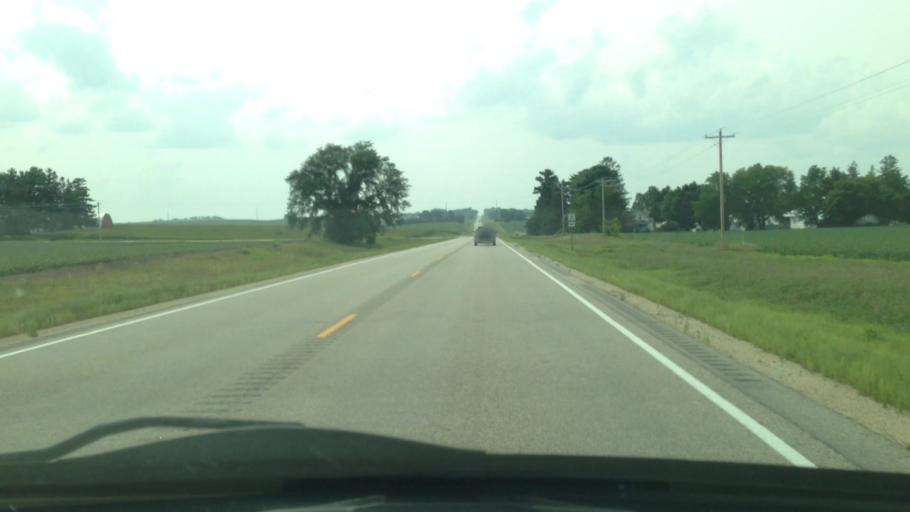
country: US
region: Minnesota
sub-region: Wabasha County
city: Elgin
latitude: 44.1658
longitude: -92.3558
